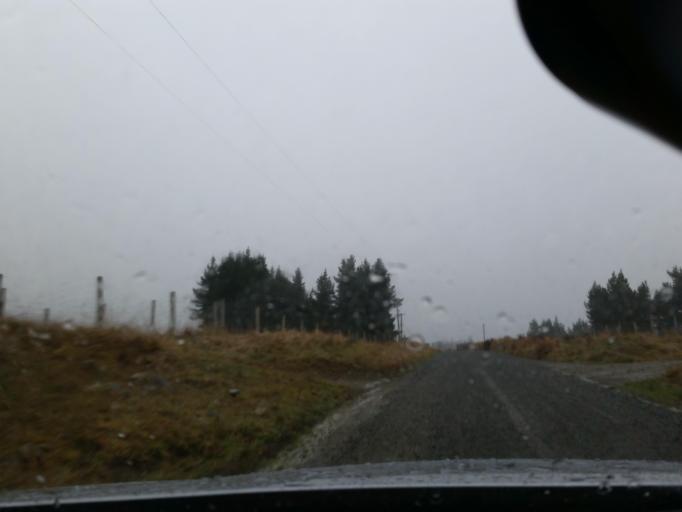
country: NZ
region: Southland
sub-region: Southland District
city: Te Anau
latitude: -45.5796
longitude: 168.0638
